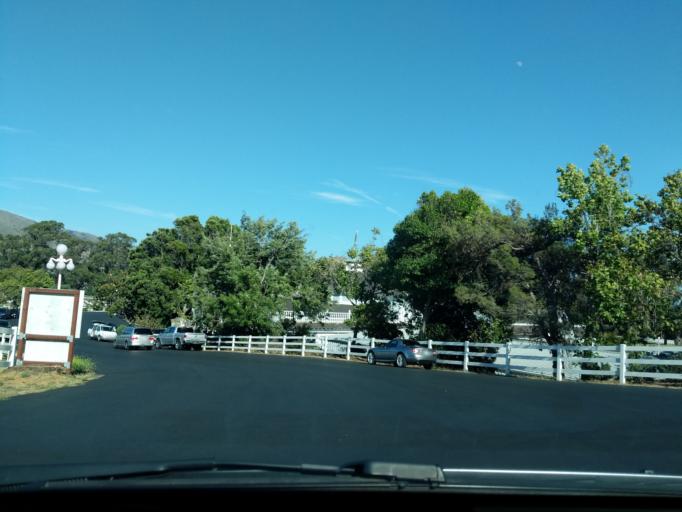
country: US
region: California
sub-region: San Luis Obispo County
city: San Luis Obispo
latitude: 35.2677
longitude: -120.6756
